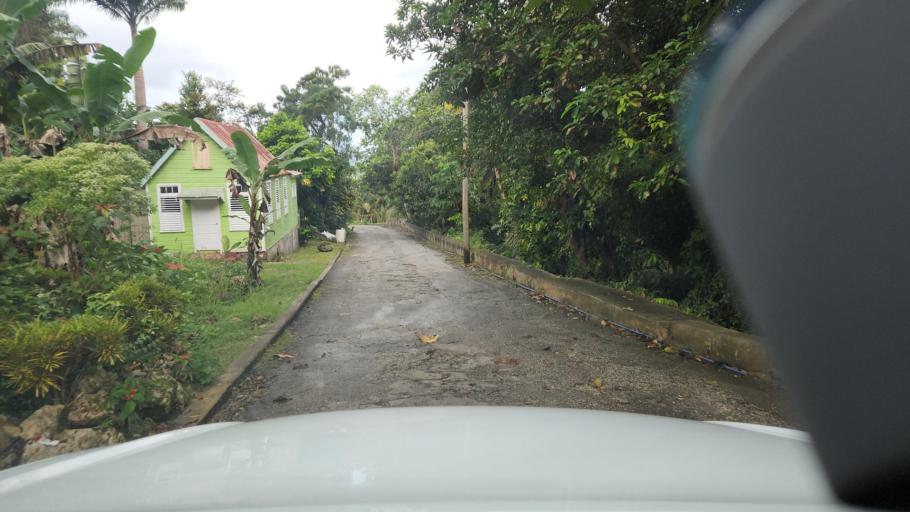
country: BB
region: Saint Joseph
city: Bathsheba
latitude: 13.1988
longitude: -59.5393
